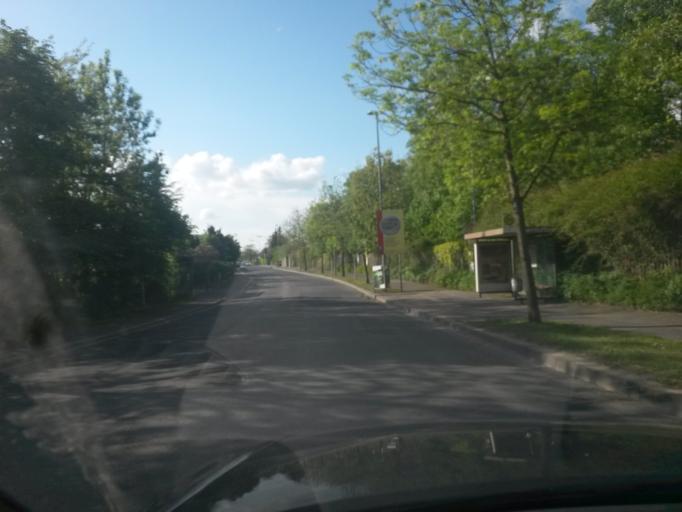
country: DE
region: Bavaria
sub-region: Regierungsbezirk Unterfranken
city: Wuerzburg
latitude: 49.7877
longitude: 9.9630
